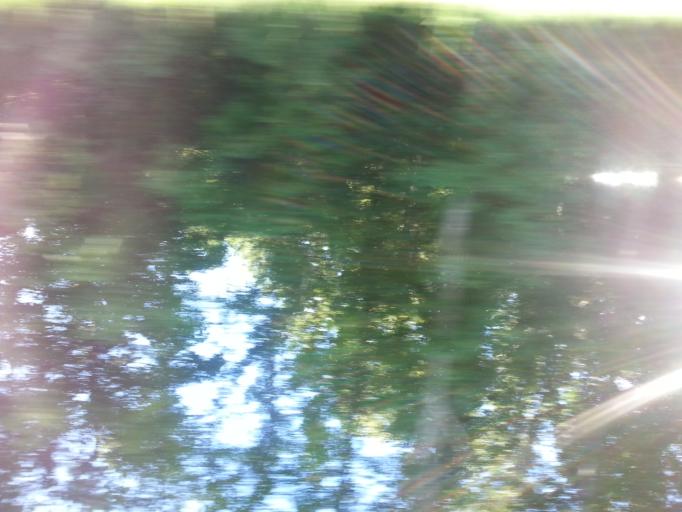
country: US
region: Alabama
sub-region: Lauderdale County
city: Killen
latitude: 34.8593
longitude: -87.5275
